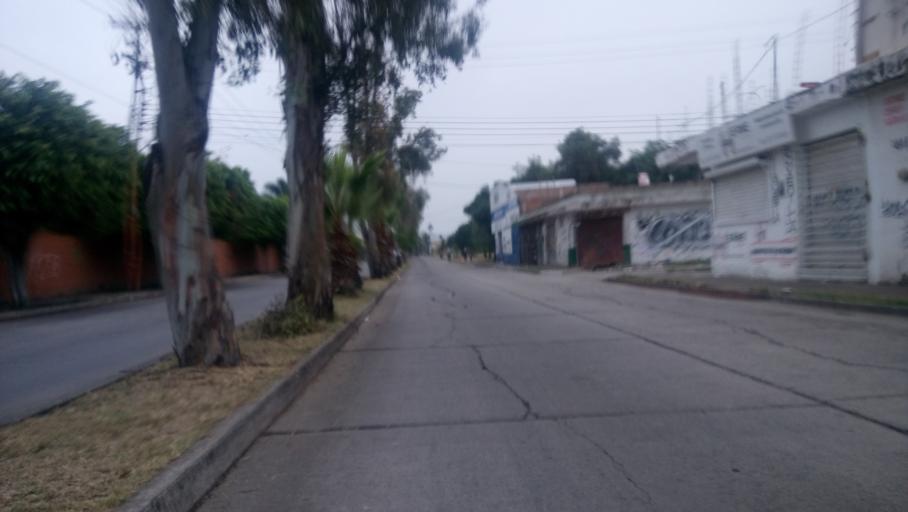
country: MX
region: Guanajuato
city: Leon
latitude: 21.1417
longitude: -101.6639
